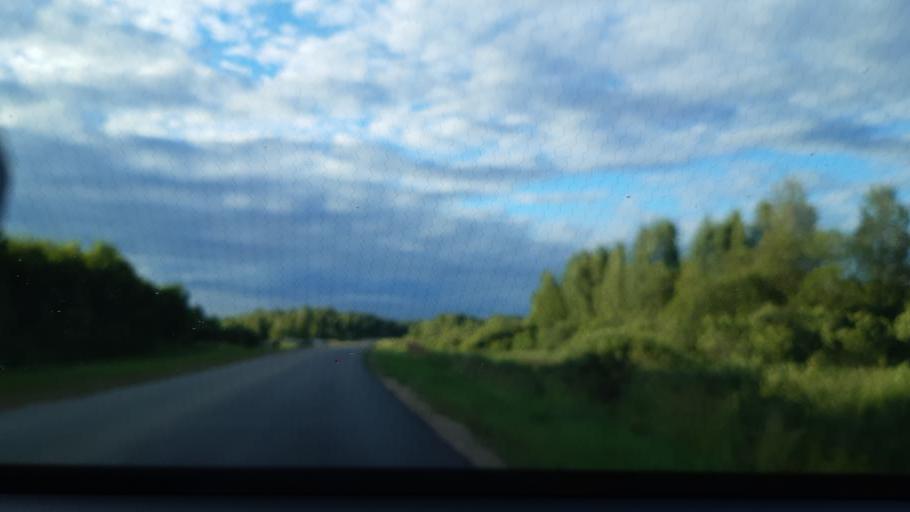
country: RU
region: Smolensk
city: Yel'nya
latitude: 54.6143
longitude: 33.1780
